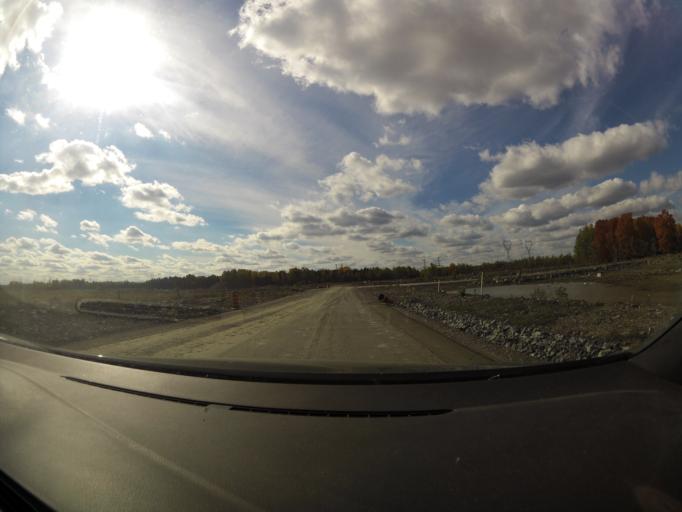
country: CA
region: Ontario
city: Bells Corners
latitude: 45.2691
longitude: -75.8961
